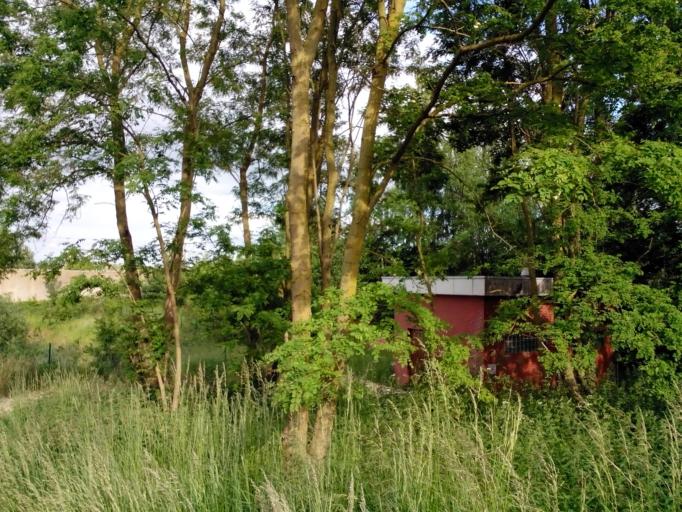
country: BE
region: Flanders
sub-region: Provincie Vlaams-Brabant
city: Bierbeek
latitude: 50.8523
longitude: 4.7352
